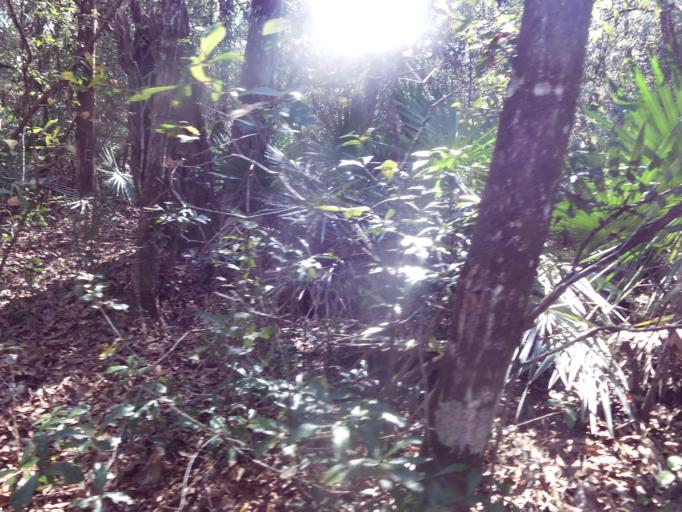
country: US
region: Florida
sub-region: Putnam County
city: Interlachen
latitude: 29.7656
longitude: -81.8295
